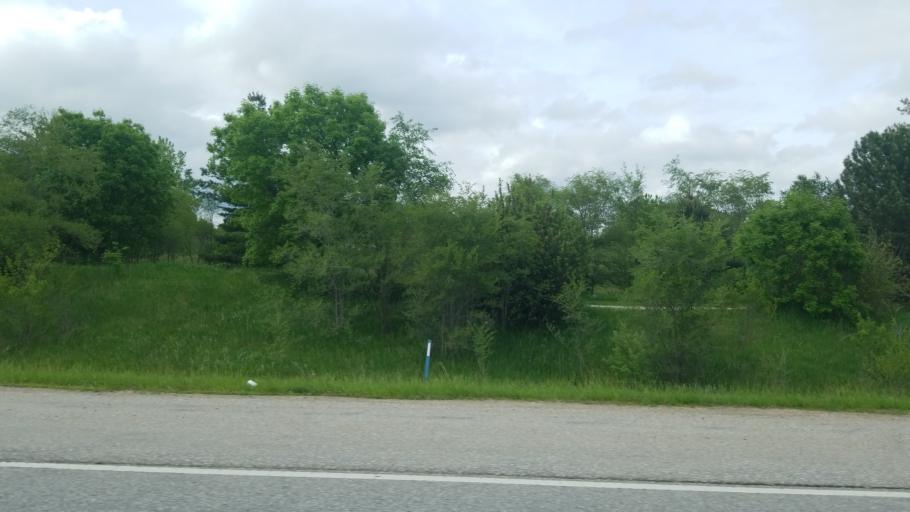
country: US
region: Nebraska
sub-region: Lancaster County
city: Lincoln
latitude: 40.8732
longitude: -96.7254
